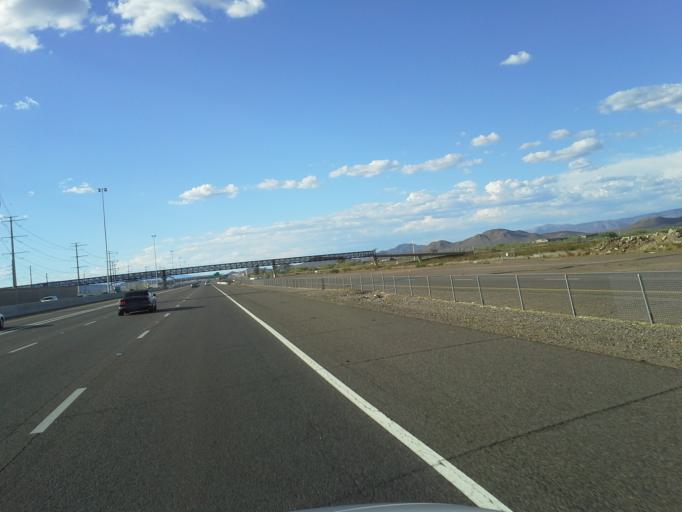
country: US
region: Arizona
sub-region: Maricopa County
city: Anthem
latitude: 33.7437
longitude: -112.1238
